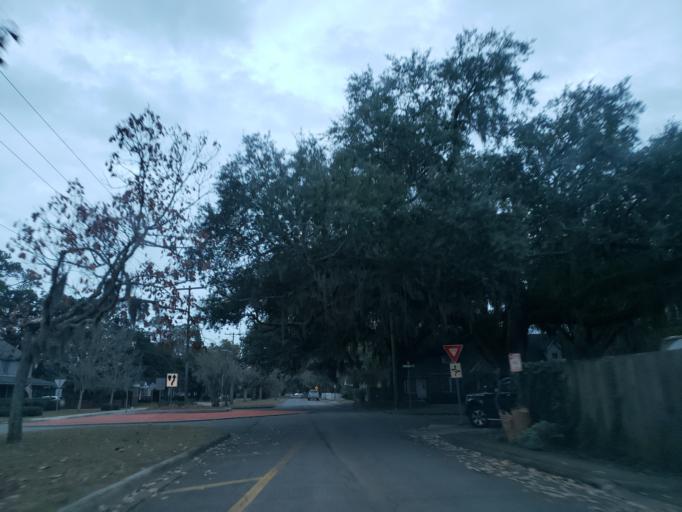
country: US
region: Georgia
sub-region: Chatham County
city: Thunderbolt
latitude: 32.0574
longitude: -81.0647
